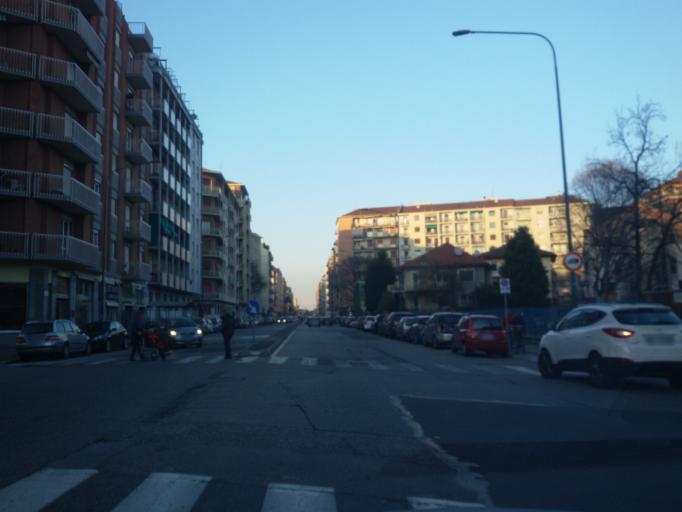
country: IT
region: Piedmont
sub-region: Provincia di Torino
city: Lesna
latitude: 45.0452
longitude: 7.6406
